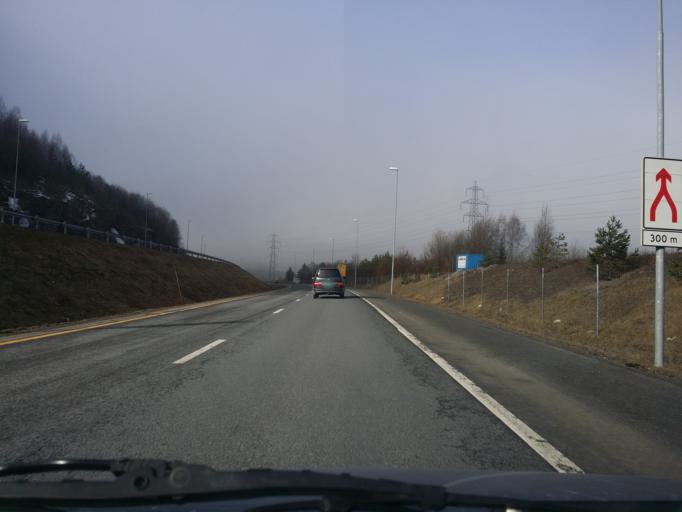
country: NO
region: Buskerud
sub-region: Nedre Eiker
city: Mjondalen
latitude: 59.7468
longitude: 10.0550
